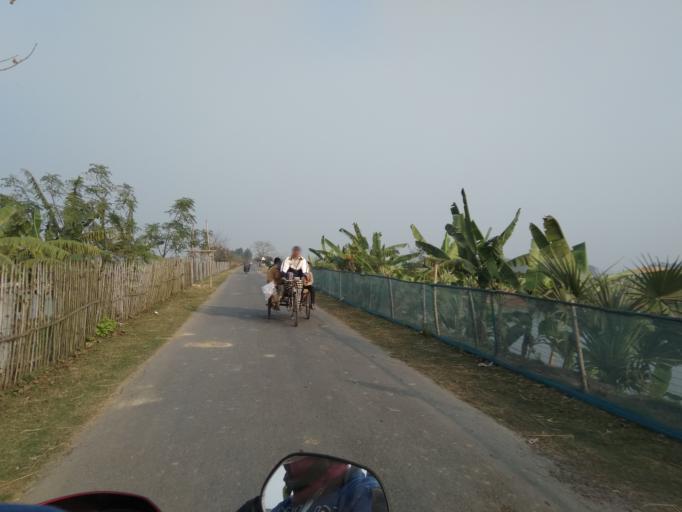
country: BD
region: Rajshahi
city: Par Naogaon
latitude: 24.4987
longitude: 89.1588
